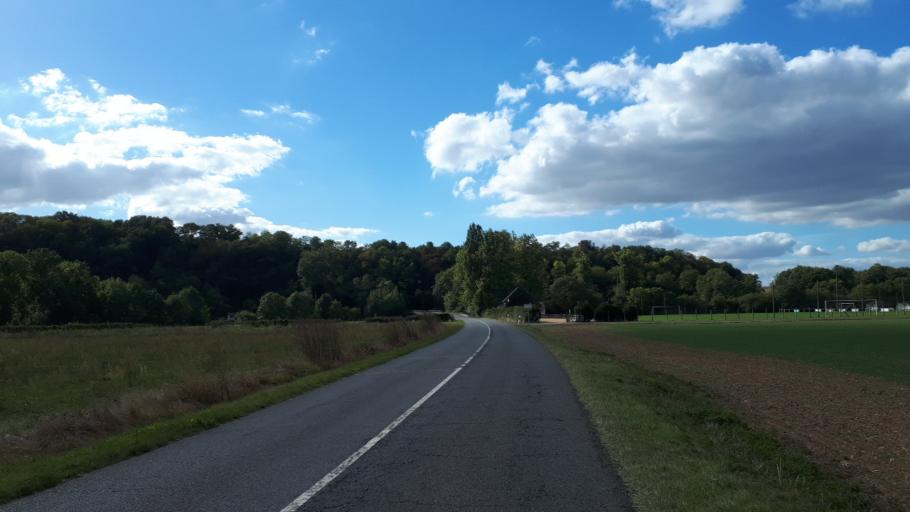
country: FR
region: Centre
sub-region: Departement du Loir-et-Cher
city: Villiers-sur-Loir
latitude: 47.7933
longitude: 0.9577
